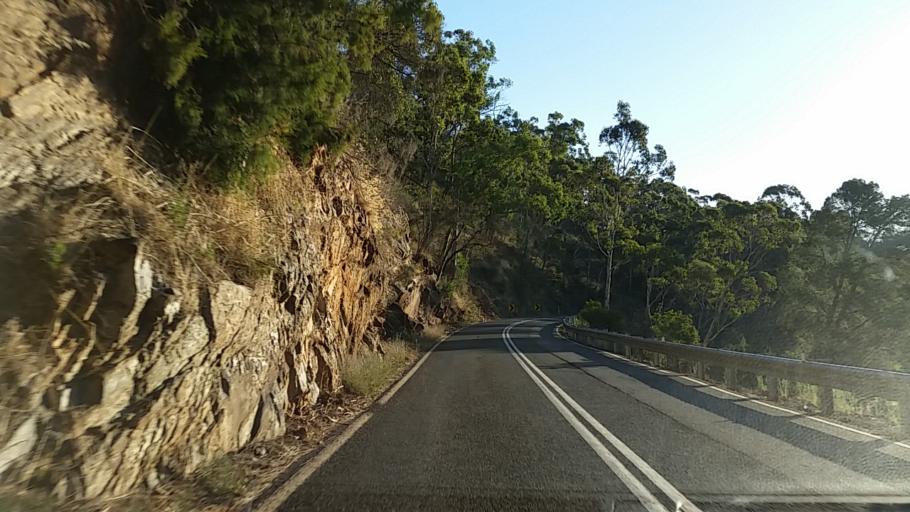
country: AU
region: South Australia
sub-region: Adelaide Hills
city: Gumeracha
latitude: -34.8425
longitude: 138.8406
